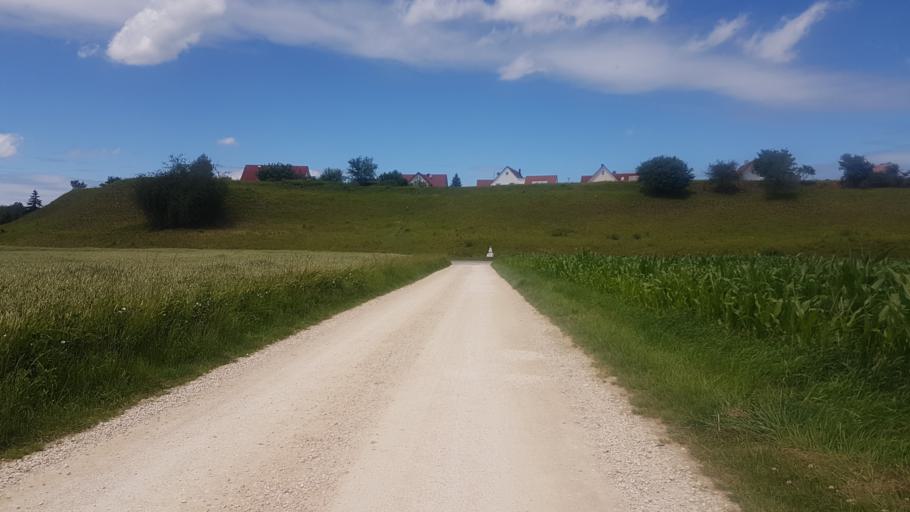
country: DE
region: Bavaria
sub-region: Swabia
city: Hochstadt an der Donau
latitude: 48.5894
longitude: 10.5370
